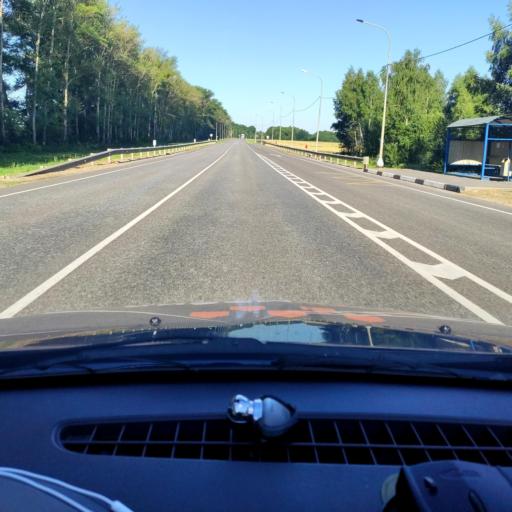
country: RU
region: Orjol
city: Pokrovskoye
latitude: 52.6199
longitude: 36.7523
